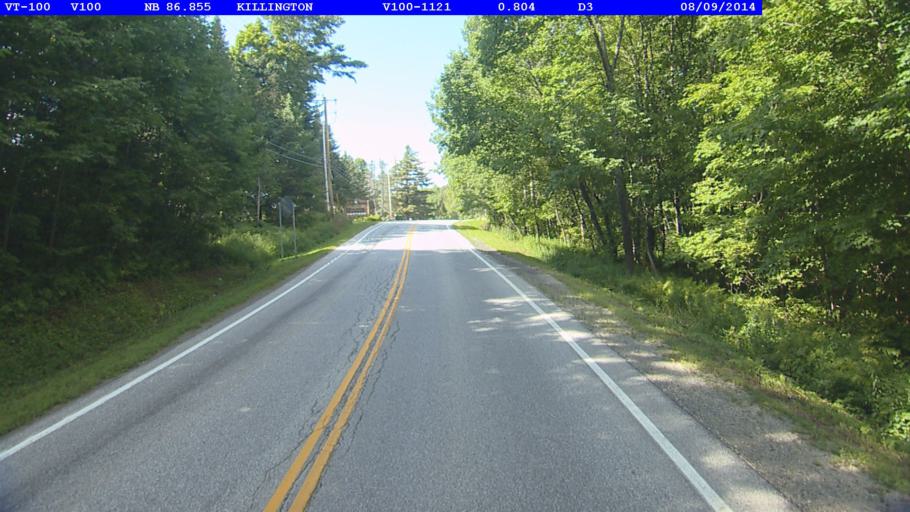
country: US
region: Vermont
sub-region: Rutland County
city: Rutland
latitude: 43.6782
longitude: -72.8105
